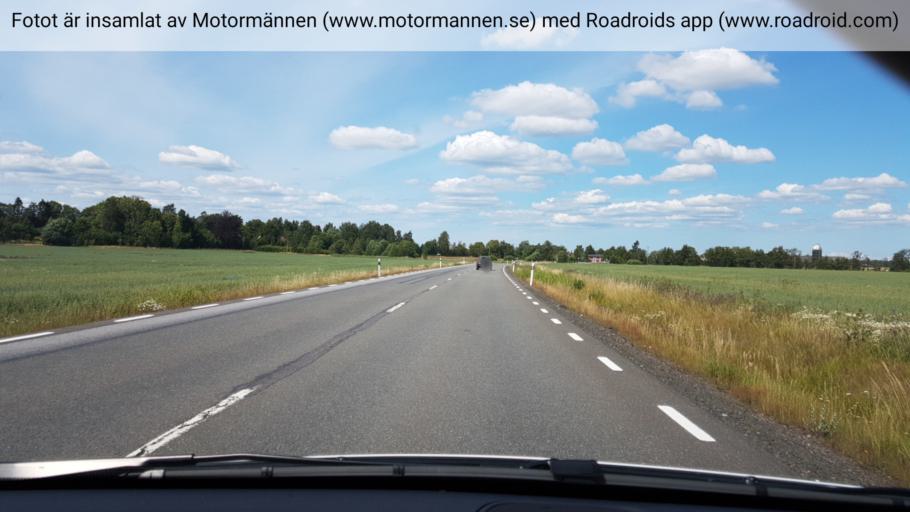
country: SE
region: Vaestra Goetaland
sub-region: Toreboda Kommun
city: Toereboda
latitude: 58.5718
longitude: 14.1011
